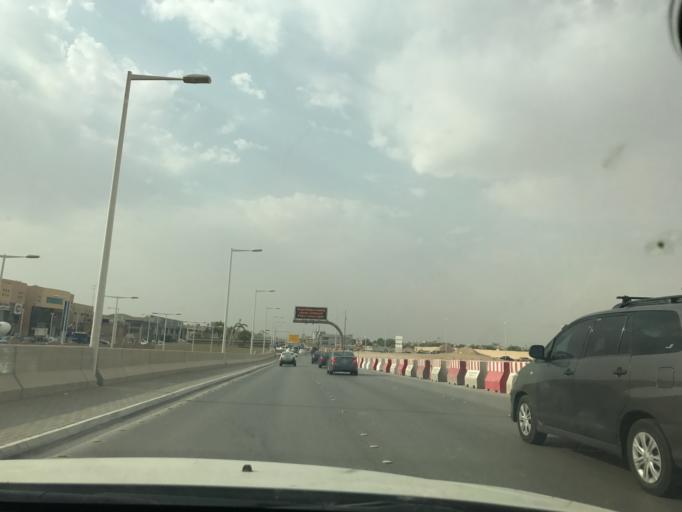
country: SA
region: Ar Riyad
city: Riyadh
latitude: 24.7193
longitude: 46.6942
